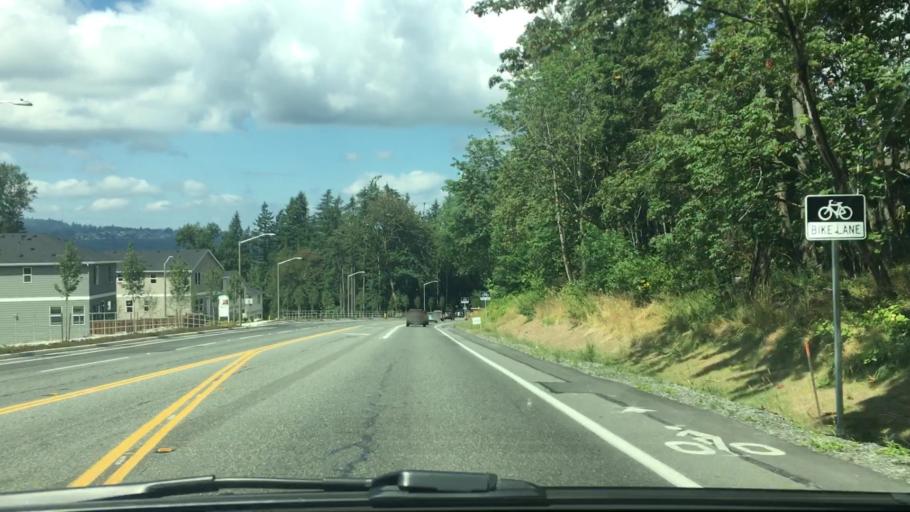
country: US
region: Washington
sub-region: King County
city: City of Sammamish
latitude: 47.5675
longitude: -122.0427
